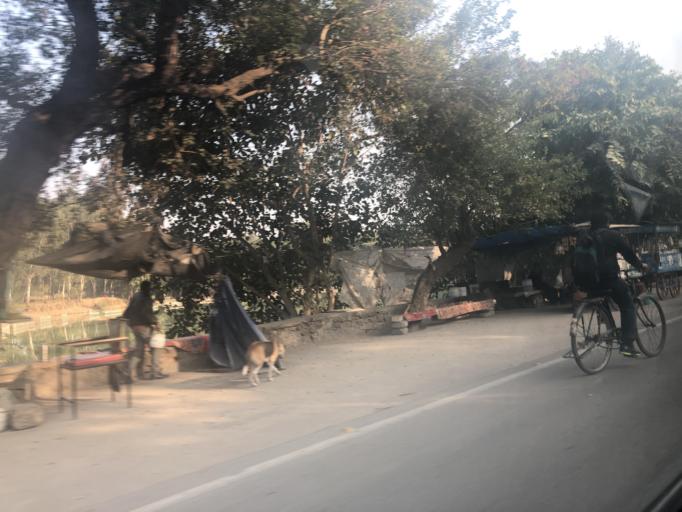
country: IN
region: Haryana
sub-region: Gurgaon
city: Gurgaon
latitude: 28.5559
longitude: 77.0056
